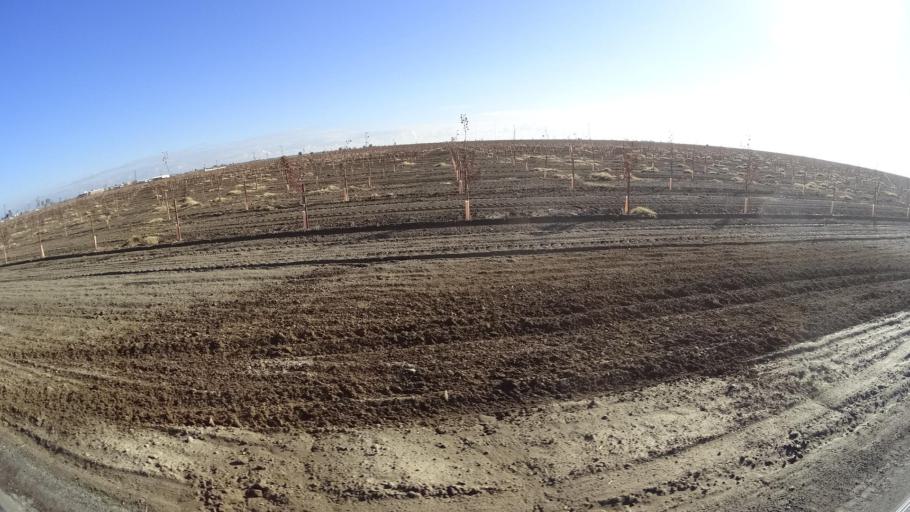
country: US
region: California
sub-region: Kern County
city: Delano
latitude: 35.7591
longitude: -119.3119
